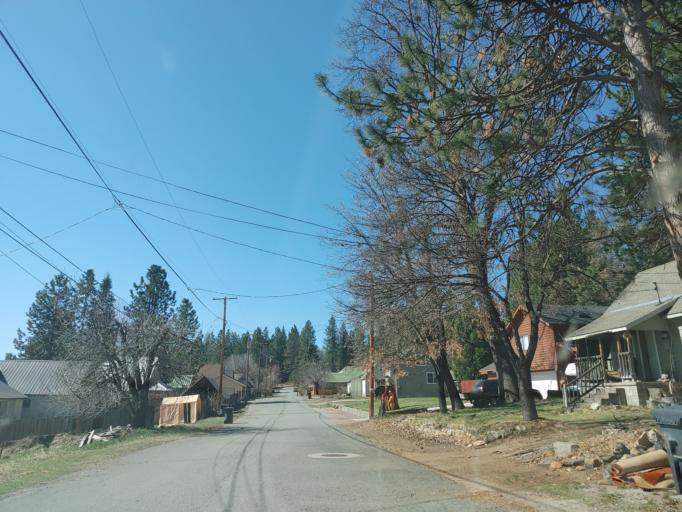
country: US
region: California
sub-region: Siskiyou County
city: McCloud
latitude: 41.2621
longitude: -122.1412
